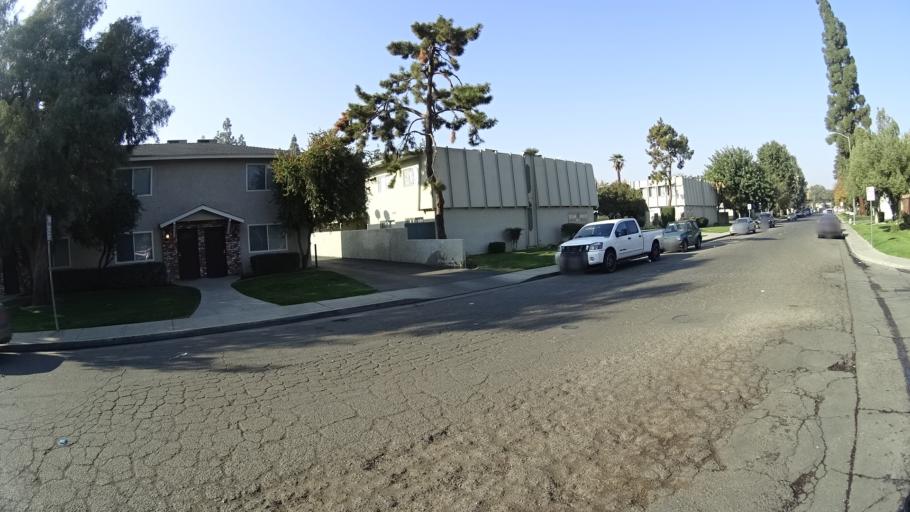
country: US
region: California
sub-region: Kern County
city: Bakersfield
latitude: 35.3493
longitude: -119.0589
